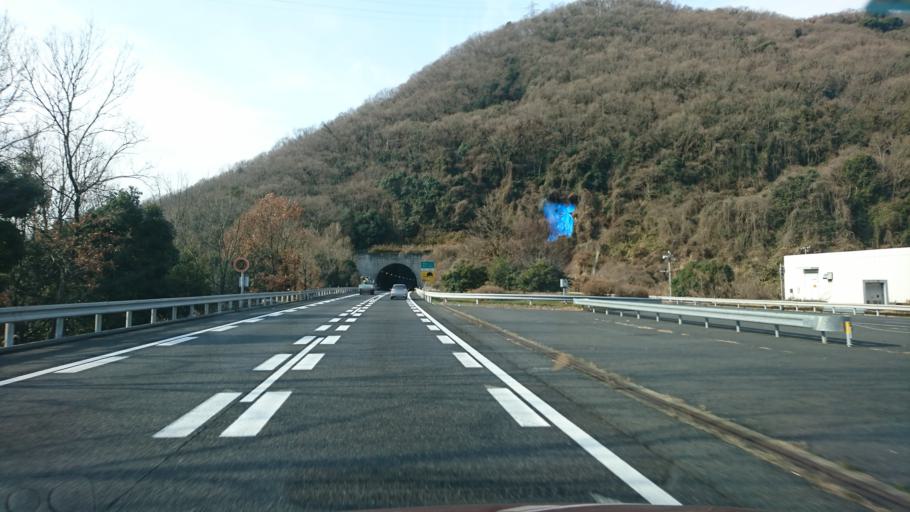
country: JP
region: Okayama
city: Okayama-shi
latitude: 34.7322
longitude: 133.9804
